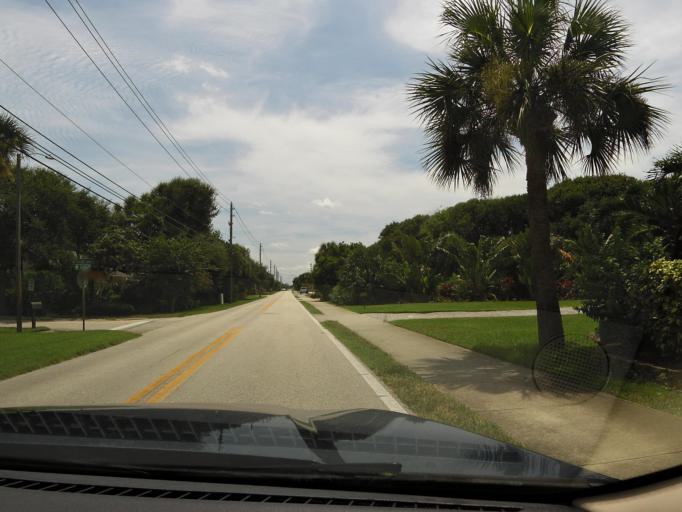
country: US
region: Florida
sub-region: Volusia County
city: Ponce Inlet
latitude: 29.1068
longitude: -80.9454
